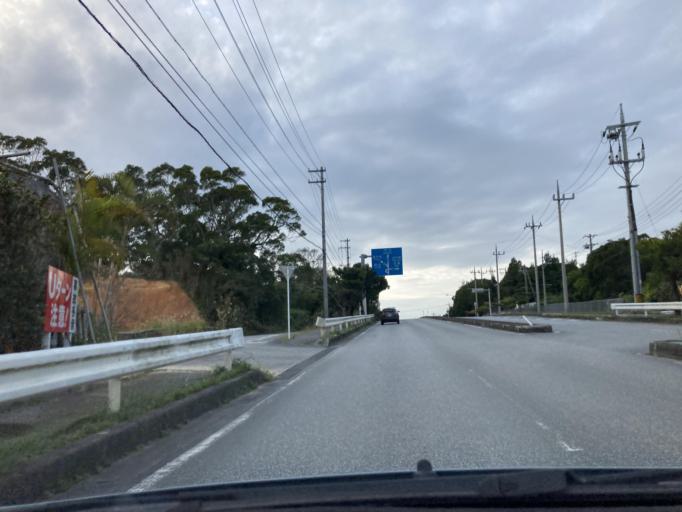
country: JP
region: Okinawa
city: Ishikawa
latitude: 26.4363
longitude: 127.8102
